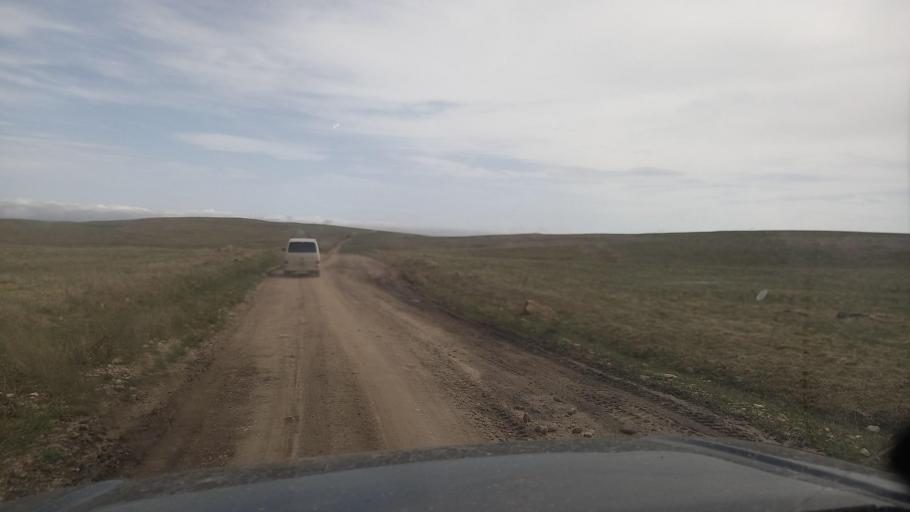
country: RU
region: Stavropol'skiy
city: Kislovodsk
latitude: 43.7533
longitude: 42.7474
